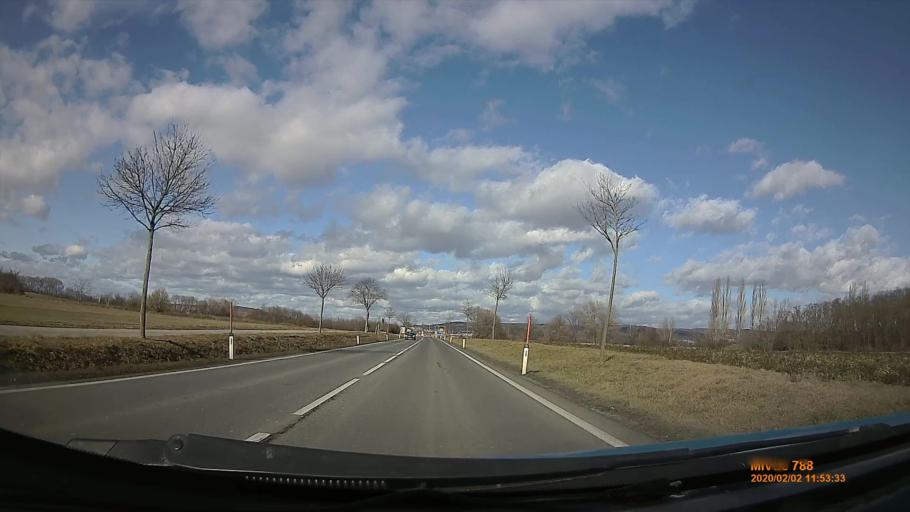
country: AT
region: Burgenland
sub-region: Eisenstadt-Umgebung
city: Wulkaprodersdorf
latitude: 47.7855
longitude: 16.5174
